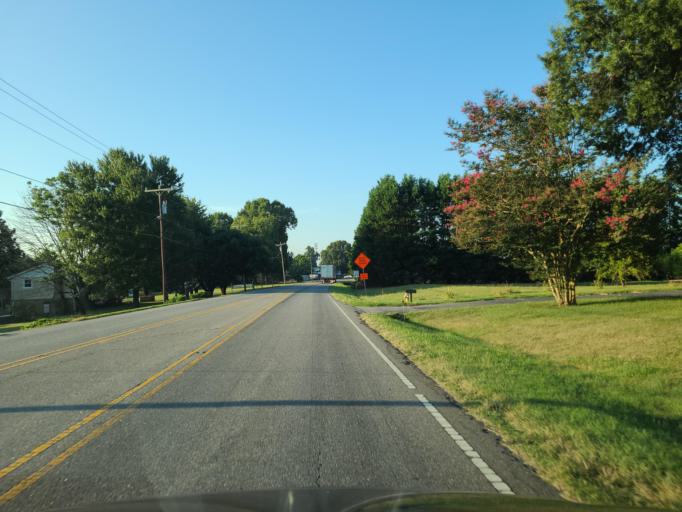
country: US
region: North Carolina
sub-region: Catawba County
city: Mountain View
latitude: 35.6627
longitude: -81.3810
